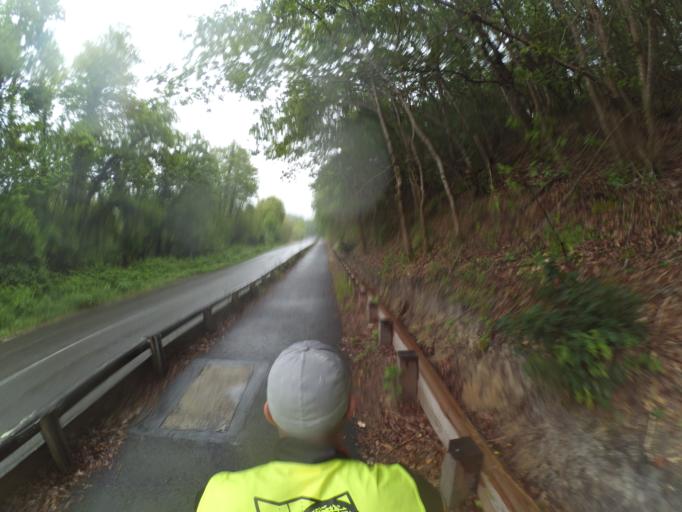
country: FR
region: Aquitaine
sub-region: Departement des Landes
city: Mimizan
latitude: 44.2331
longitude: -1.2237
